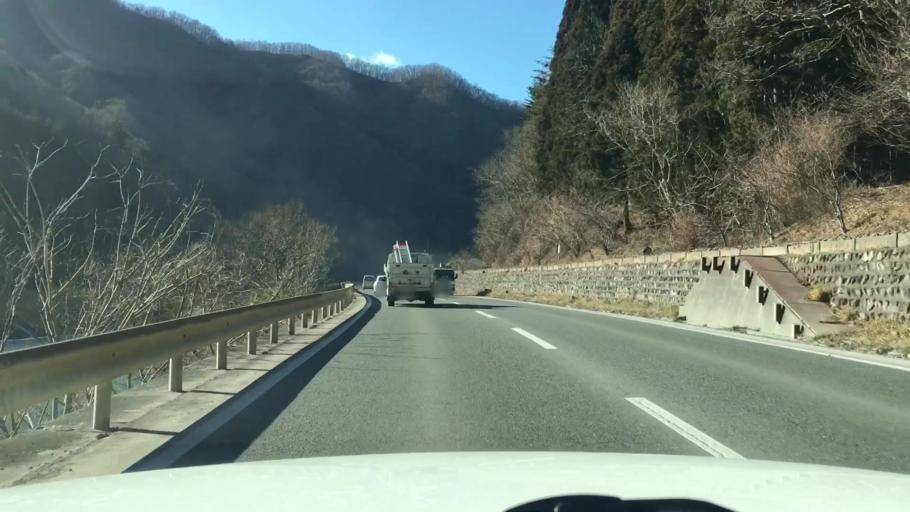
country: JP
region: Iwate
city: Miyako
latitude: 39.6228
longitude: 141.8302
